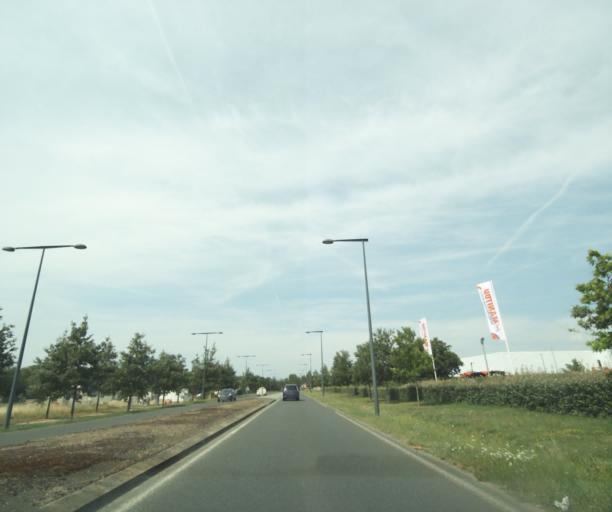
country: FR
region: Centre
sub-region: Departement d'Indre-et-Loire
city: Montbazon
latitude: 47.2763
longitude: 0.7097
